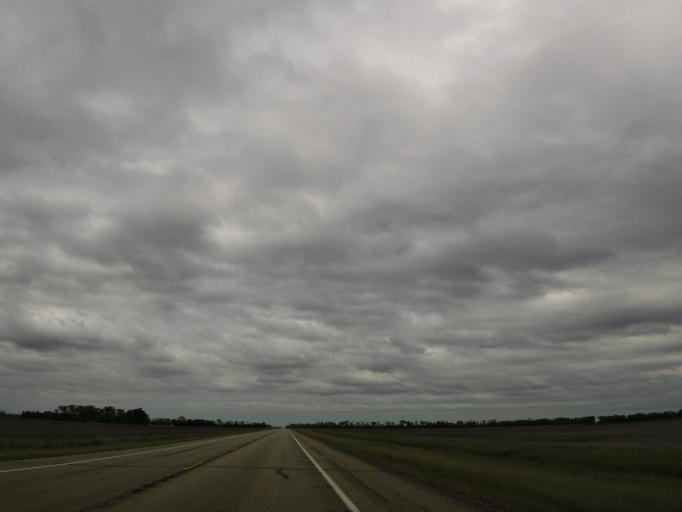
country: US
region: North Dakota
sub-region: Walsh County
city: Grafton
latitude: 48.5248
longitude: -97.4476
